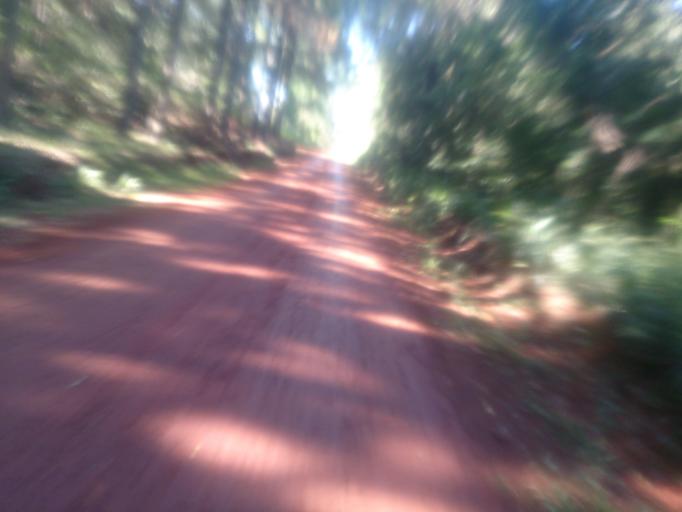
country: AR
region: Misiones
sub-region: Departamento de Obera
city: Obera
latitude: -27.4365
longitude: -55.1150
